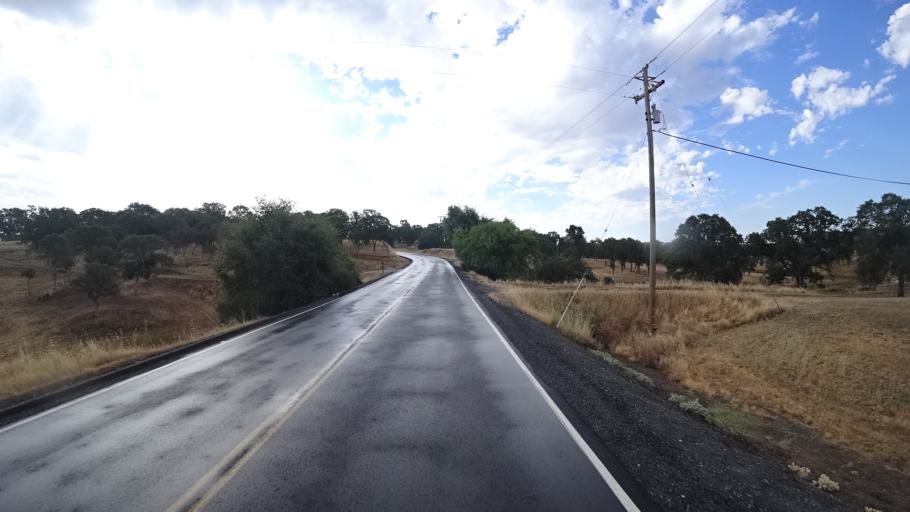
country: US
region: California
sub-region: Calaveras County
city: Copperopolis
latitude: 37.9141
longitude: -120.6225
